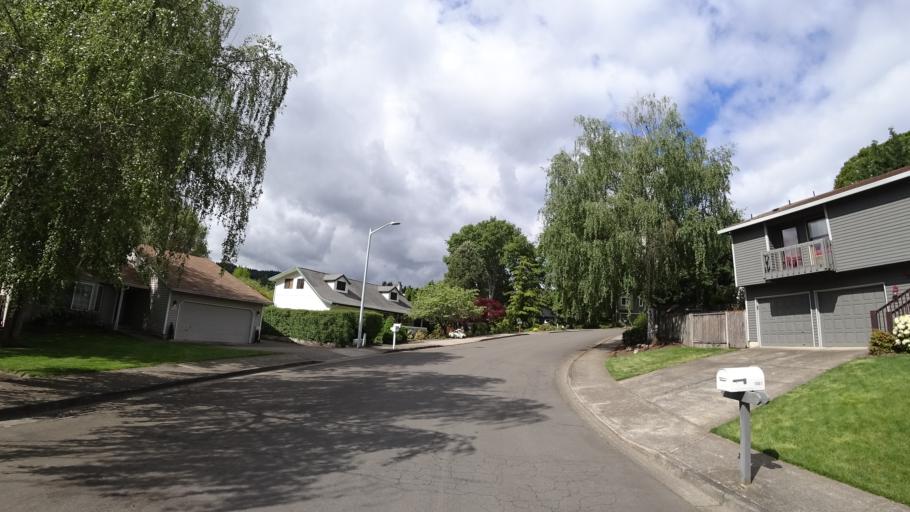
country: US
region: Oregon
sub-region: Washington County
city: Aloha
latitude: 45.4625
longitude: -122.8432
